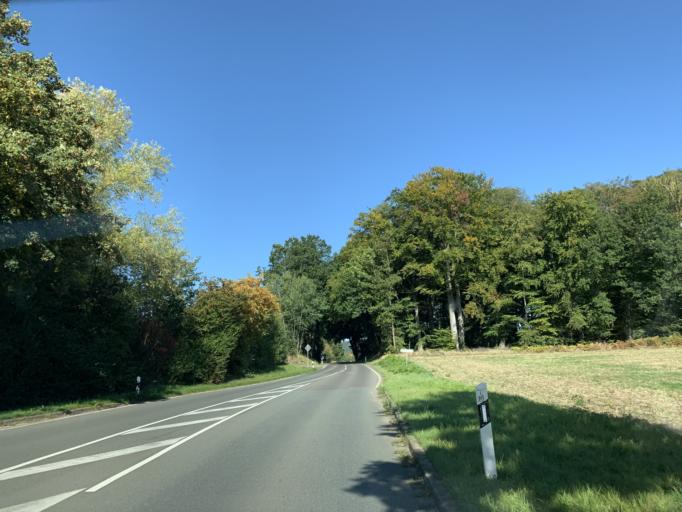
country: DE
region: North Rhine-Westphalia
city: Porta Westfalica
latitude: 52.2165
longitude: 8.9530
